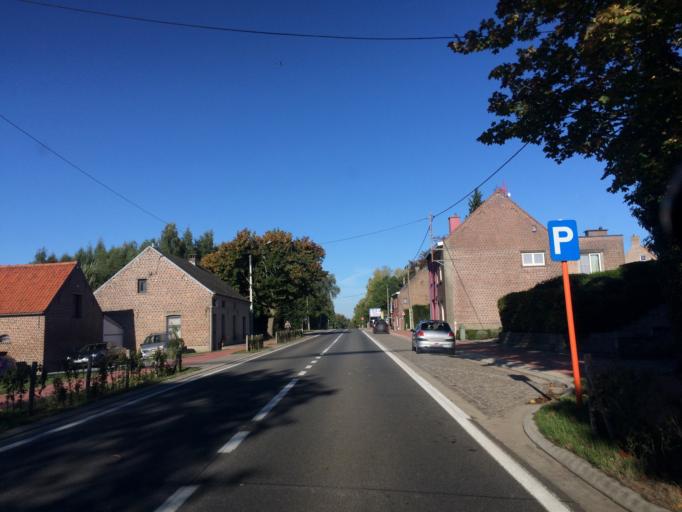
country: BE
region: Flanders
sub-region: Provincie Vlaams-Brabant
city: Merchtem
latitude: 50.9304
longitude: 4.2579
